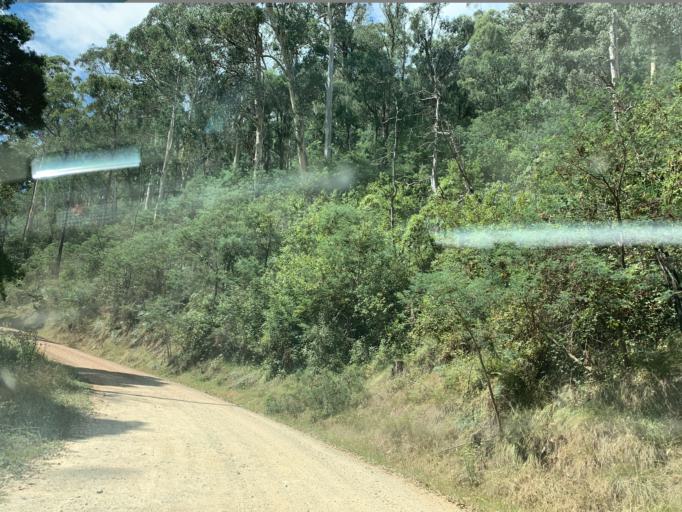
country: AU
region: Victoria
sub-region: Mansfield
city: Mansfield
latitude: -37.0946
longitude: 146.5185
